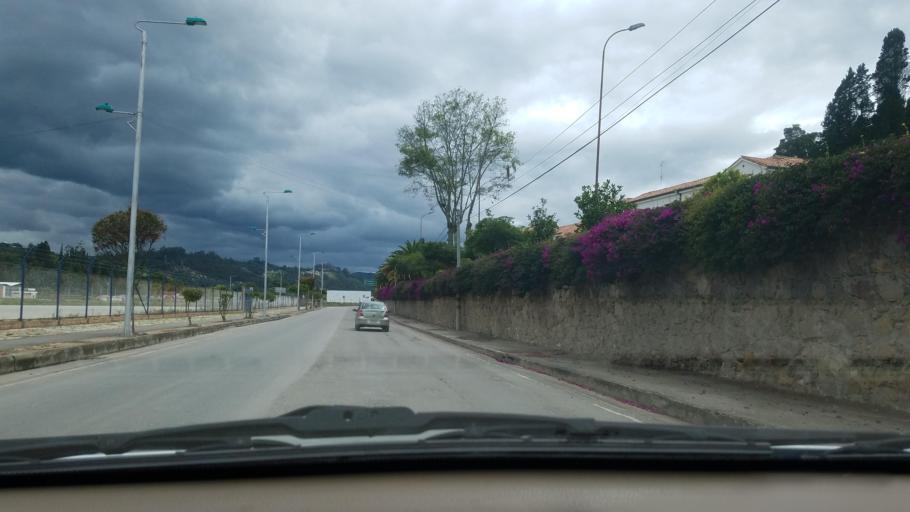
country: CO
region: Boyaca
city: Paipa
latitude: 5.7623
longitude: -73.1105
